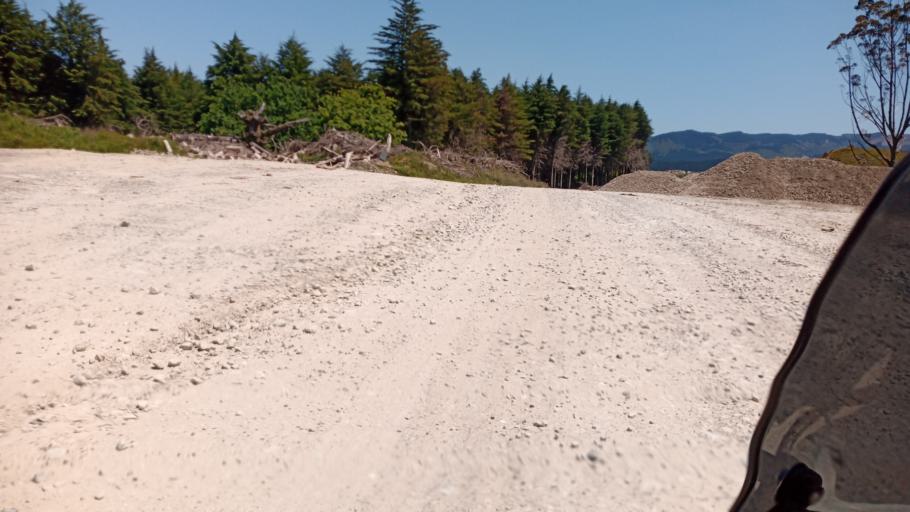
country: NZ
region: Gisborne
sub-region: Gisborne District
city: Gisborne
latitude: -38.2924
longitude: 178.0195
